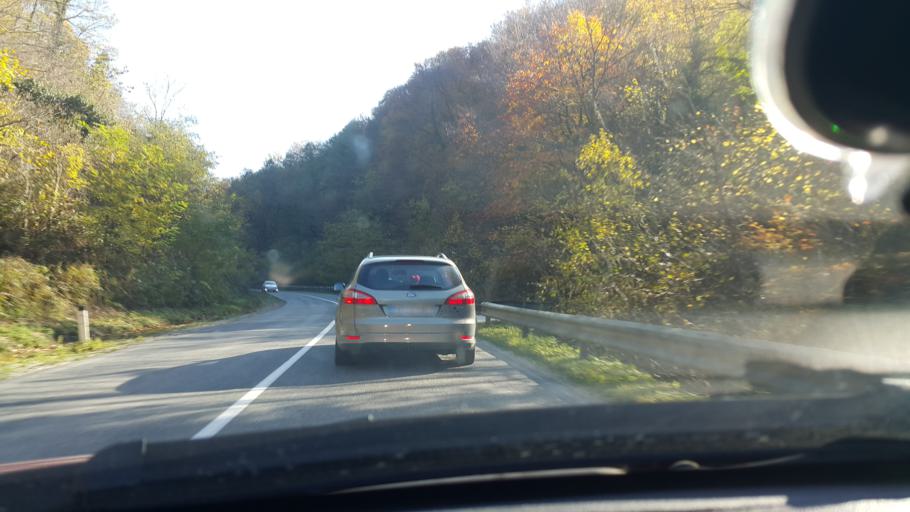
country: SI
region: Bistrica ob Sotli
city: Bistrica ob Sotli
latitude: 46.0499
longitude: 15.6665
